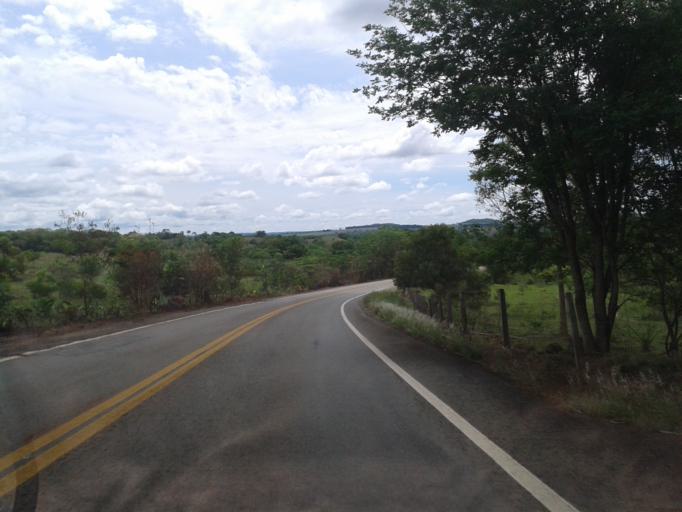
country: BR
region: Goias
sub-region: Buriti Alegre
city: Buriti Alegre
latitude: -18.1343
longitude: -49.2006
